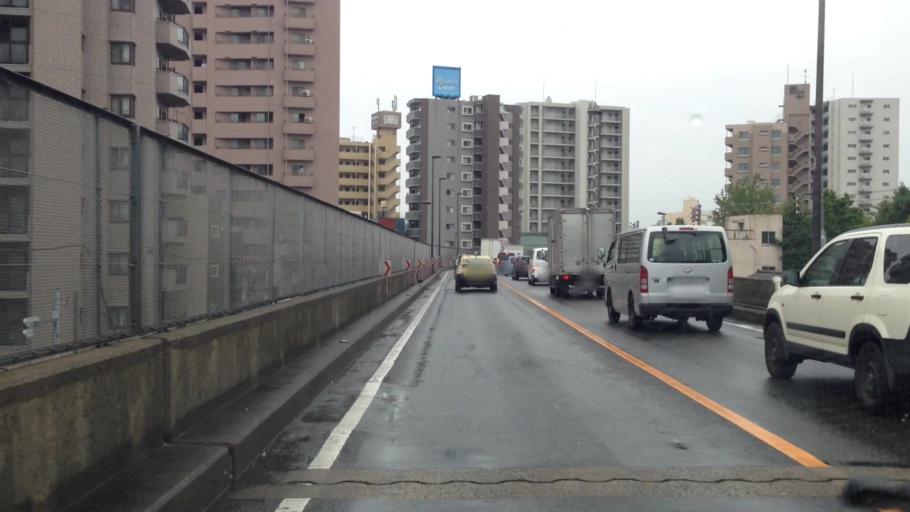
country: JP
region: Saitama
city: Soka
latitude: 35.7379
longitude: 139.7971
